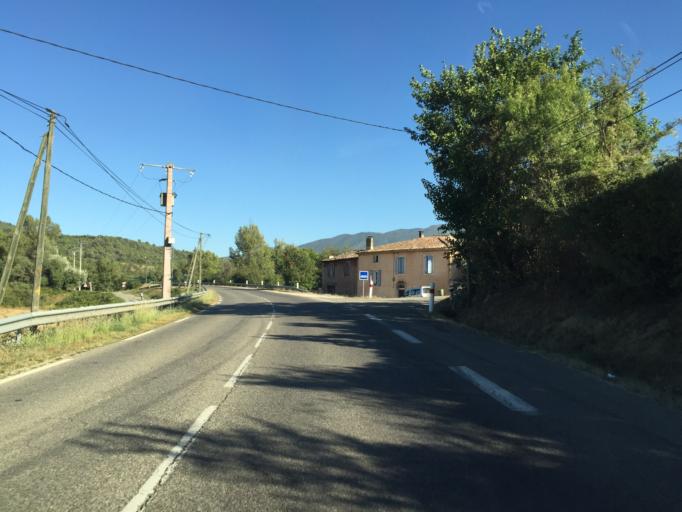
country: FR
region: Provence-Alpes-Cote d'Azur
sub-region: Departement du Vaucluse
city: Saignon
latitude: 43.8672
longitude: 5.4573
